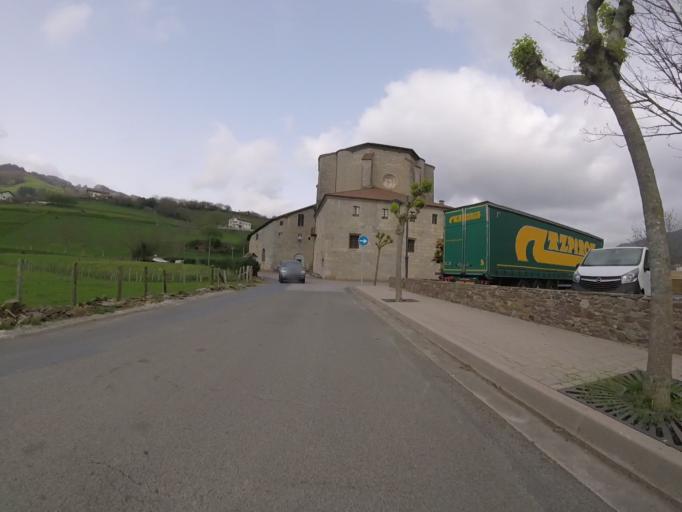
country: ES
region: Basque Country
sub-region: Provincia de Guipuzcoa
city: Berastegui
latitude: 43.1235
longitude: -1.9833
